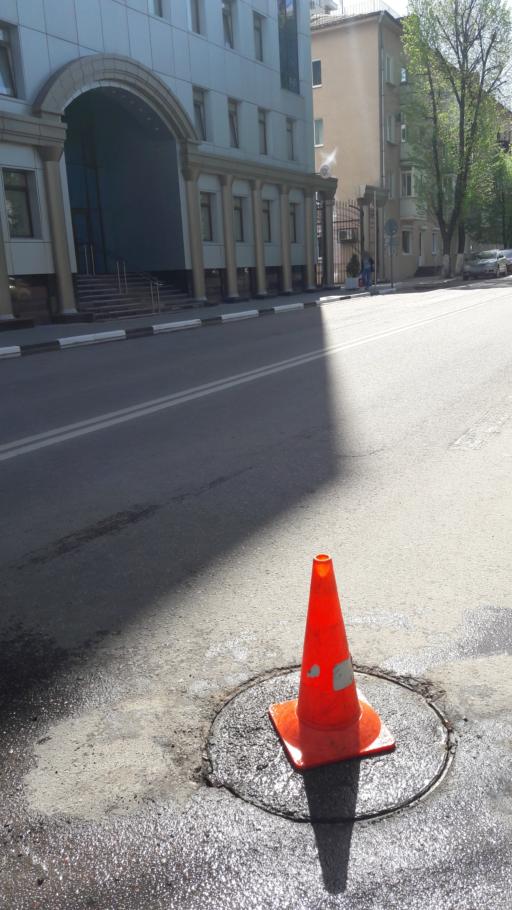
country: RU
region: Voronezj
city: Voronezh
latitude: 51.6607
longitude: 39.2079
